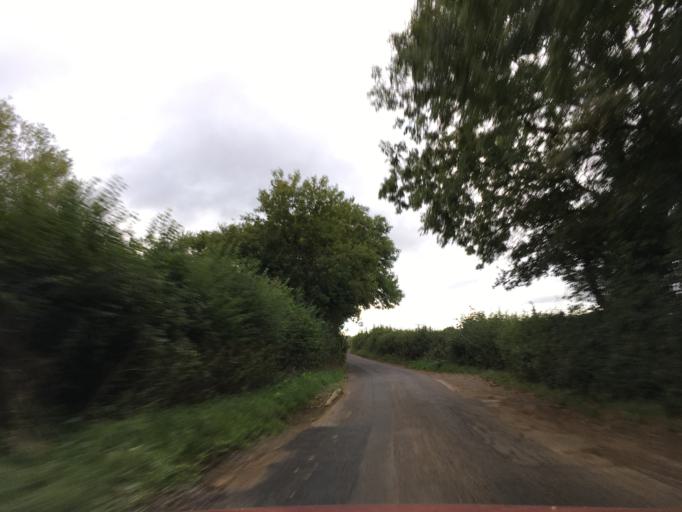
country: GB
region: England
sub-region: Wiltshire
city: Biddestone
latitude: 51.4544
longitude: -2.1998
